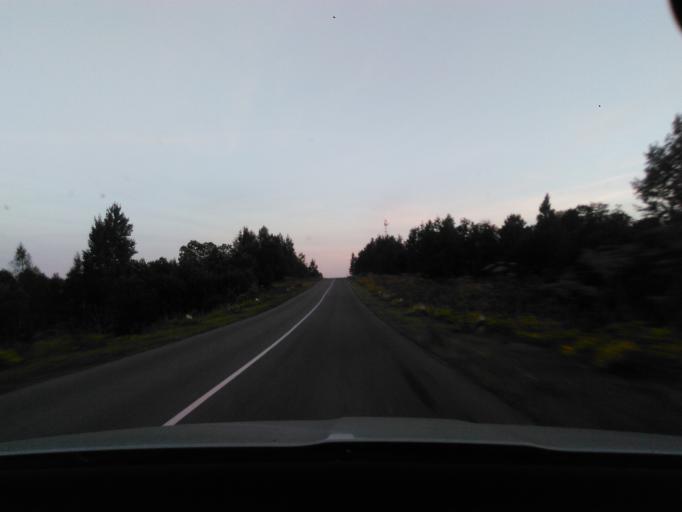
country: RU
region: Moskovskaya
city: Klin
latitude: 56.2378
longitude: 36.7526
